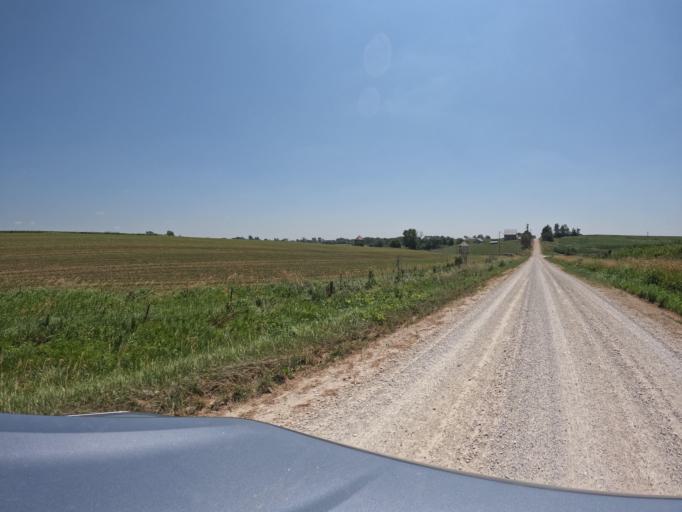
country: US
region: Iowa
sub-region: Keokuk County
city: Sigourney
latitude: 41.2664
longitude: -92.1806
